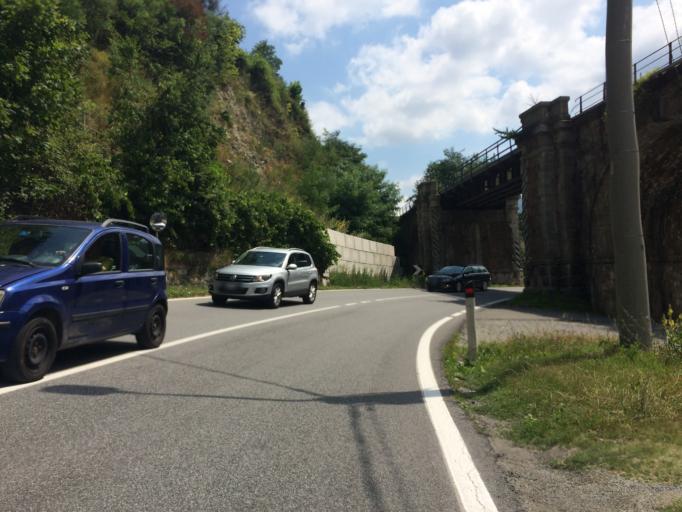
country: IT
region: Piedmont
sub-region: Provincia di Cuneo
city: Ormea
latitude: 44.1550
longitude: 7.9163
